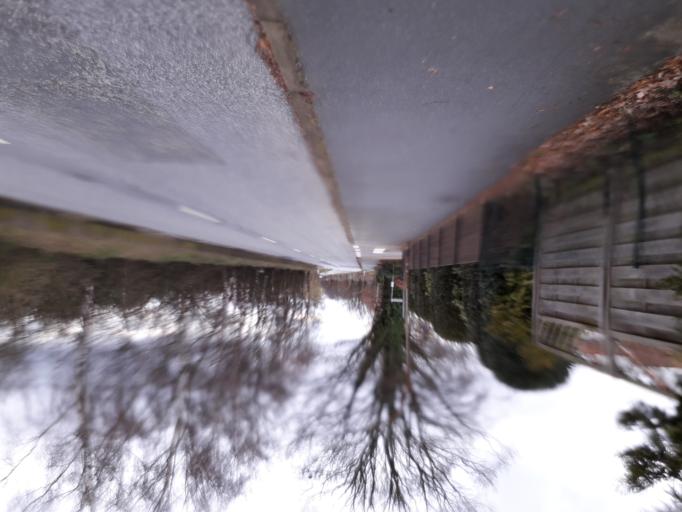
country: DE
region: Schleswig-Holstein
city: Glinde
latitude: 53.5607
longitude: 10.2097
